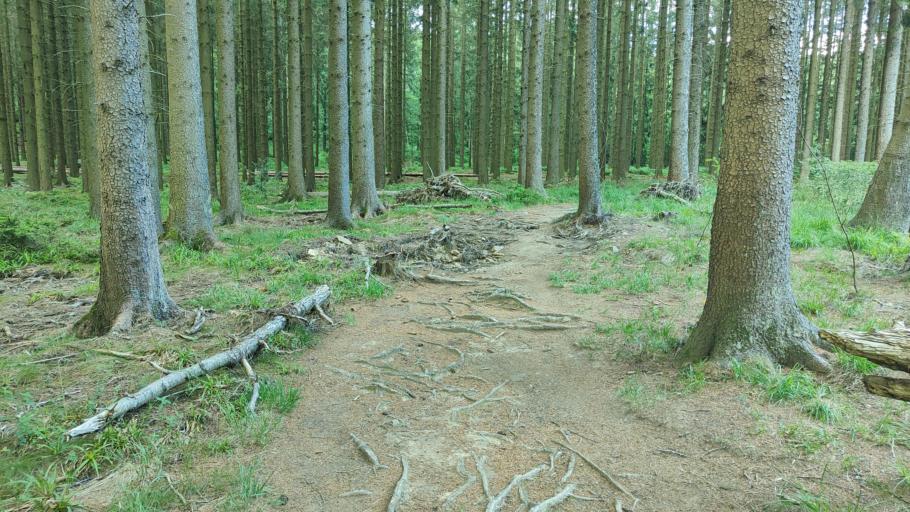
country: DE
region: North Rhine-Westphalia
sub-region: Regierungsbezirk Koln
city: Roetgen
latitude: 50.6326
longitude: 6.1560
